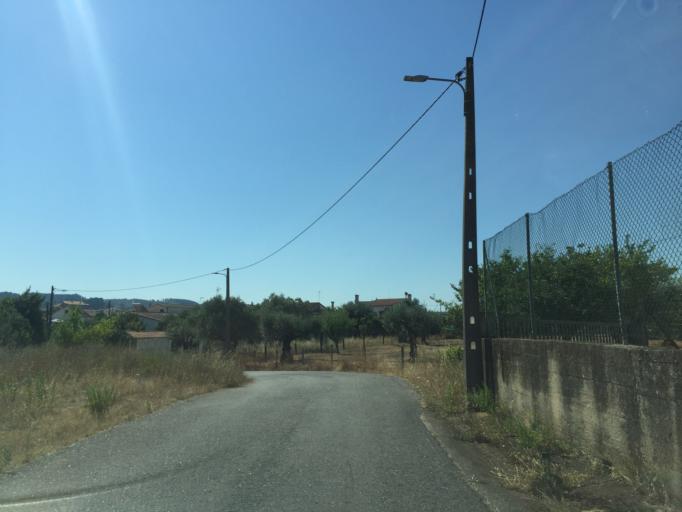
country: PT
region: Santarem
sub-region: Constancia
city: Constancia
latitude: 39.5375
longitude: -8.3169
